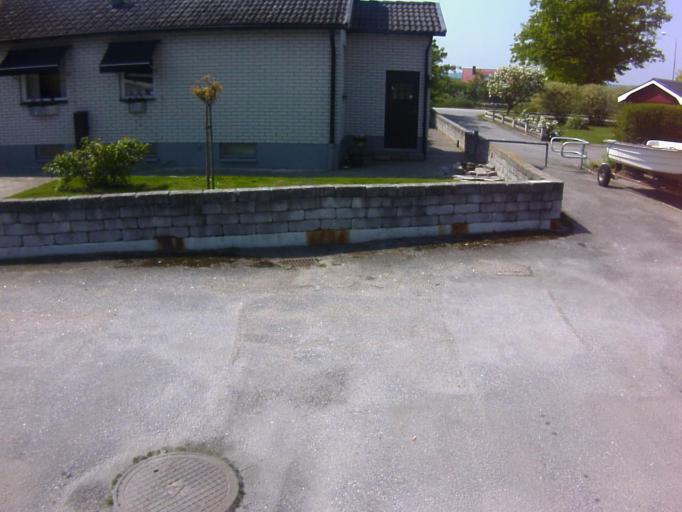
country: SE
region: Blekinge
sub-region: Karlshamns Kommun
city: Morrum
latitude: 56.1240
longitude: 14.6702
